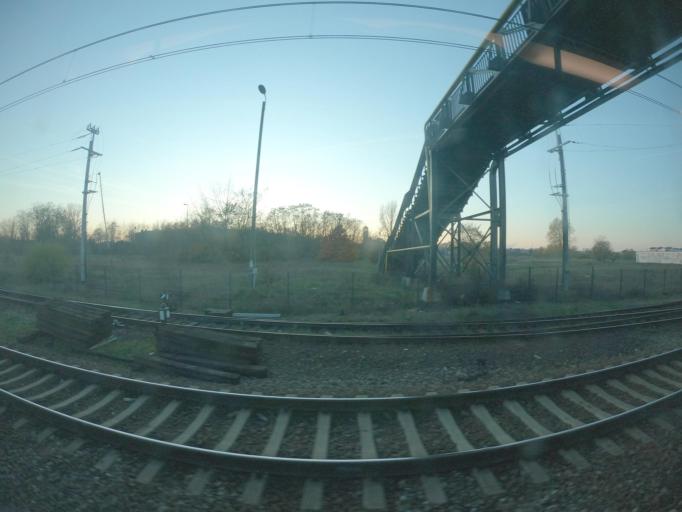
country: PL
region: Lubusz
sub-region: Powiat gorzowski
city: Kostrzyn nad Odra
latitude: 52.5981
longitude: 14.6483
